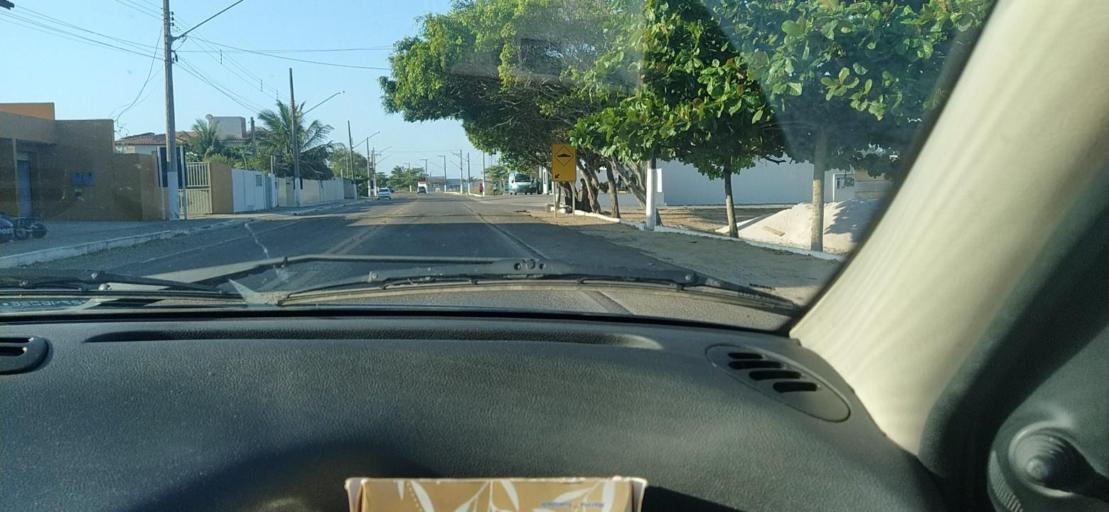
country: BR
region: Espirito Santo
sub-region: Conceicao Da Barra
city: Conceicao da Barra
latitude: -18.5795
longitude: -39.7328
